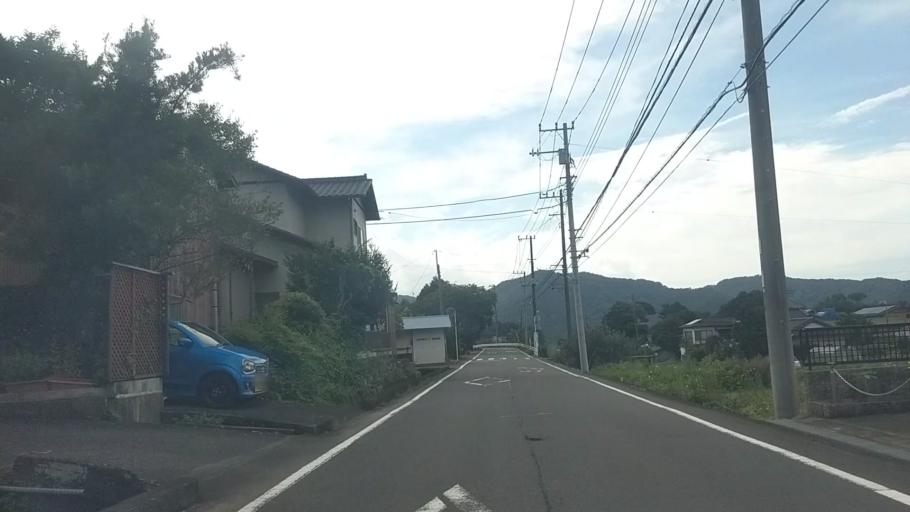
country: JP
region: Shizuoka
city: Ito
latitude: 34.9708
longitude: 138.9620
